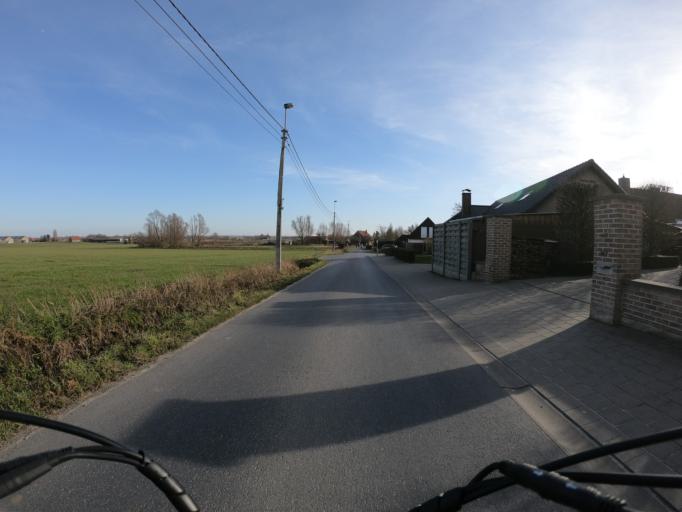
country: BE
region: Flanders
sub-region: Provincie West-Vlaanderen
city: Moorslede
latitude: 50.8886
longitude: 3.0689
